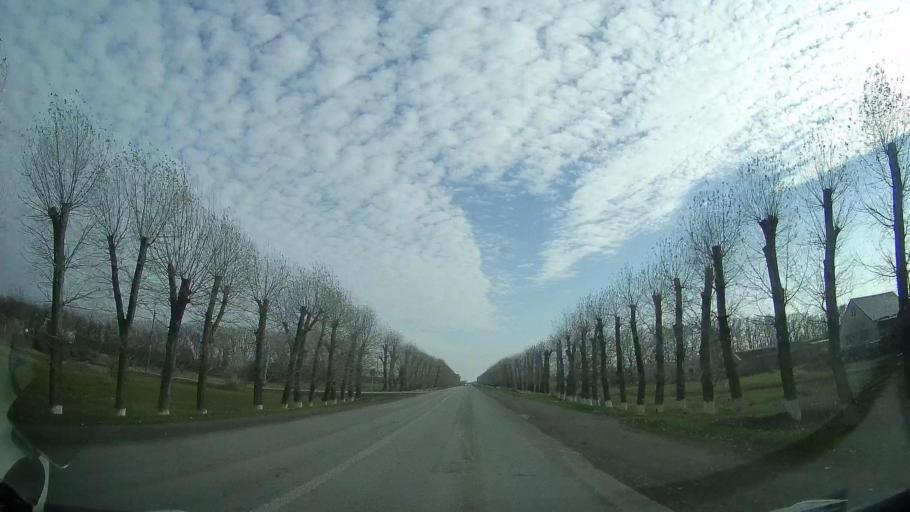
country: RU
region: Rostov
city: Tselina
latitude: 46.5282
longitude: 41.0577
